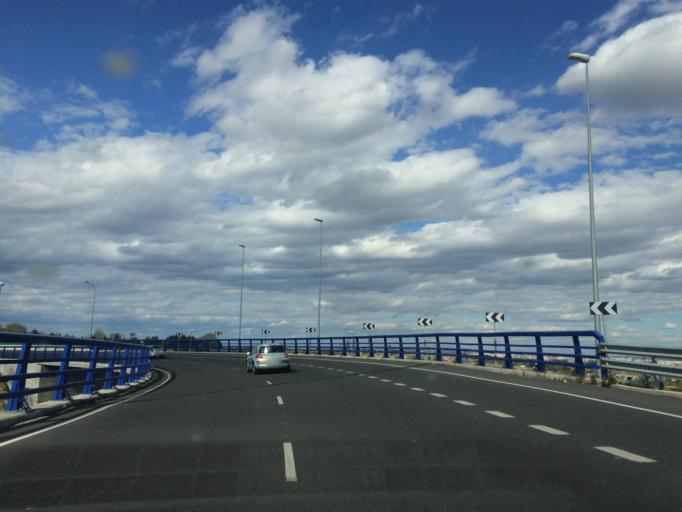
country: ES
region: Madrid
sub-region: Provincia de Madrid
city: Pozuelo de Alarcon
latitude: 40.3968
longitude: -3.8306
